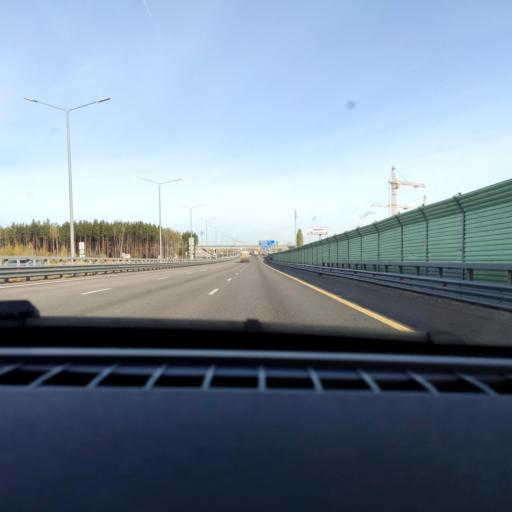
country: RU
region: Voronezj
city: Somovo
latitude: 51.7379
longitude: 39.3089
